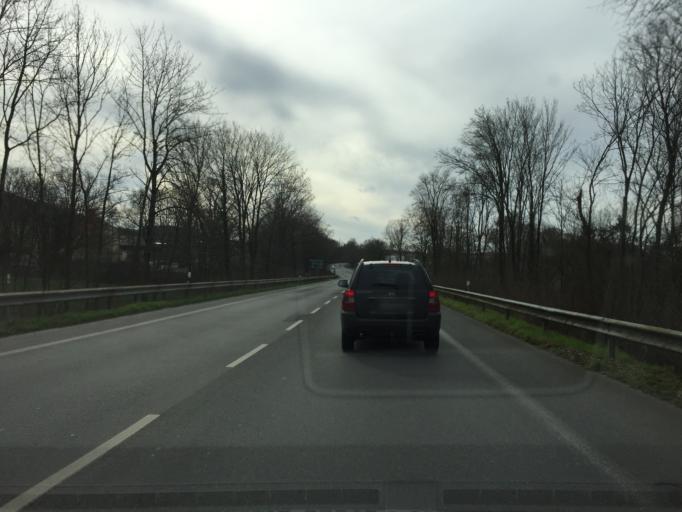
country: DE
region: North Rhine-Westphalia
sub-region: Regierungsbezirk Detmold
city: Vlotho
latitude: 52.1413
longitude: 8.8299
